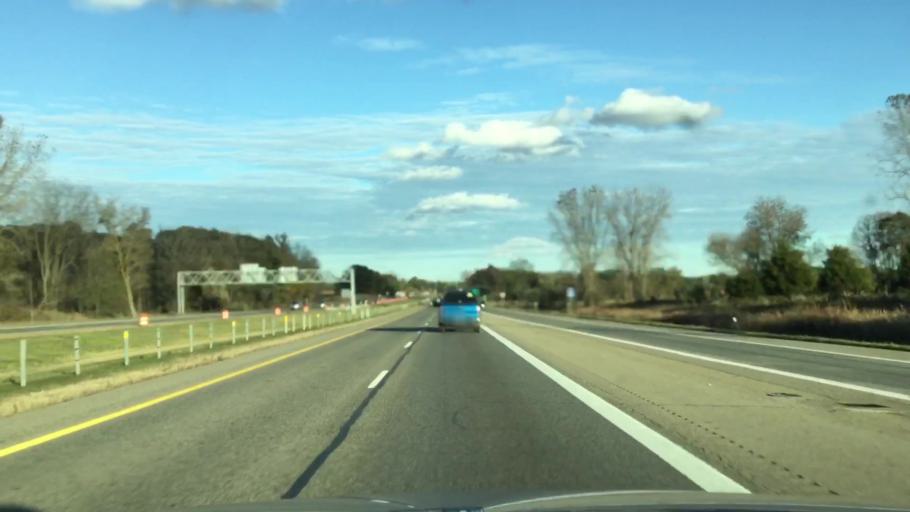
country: US
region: Michigan
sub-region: Calhoun County
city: Marshall
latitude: 42.2971
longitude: -84.9890
